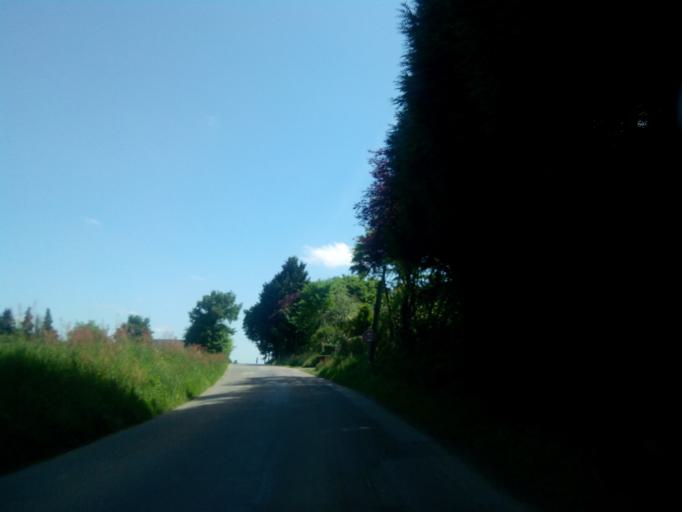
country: FR
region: Brittany
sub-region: Departement d'Ille-et-Vilaine
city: Cesson-Sevigne
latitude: 48.1391
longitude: -1.6022
